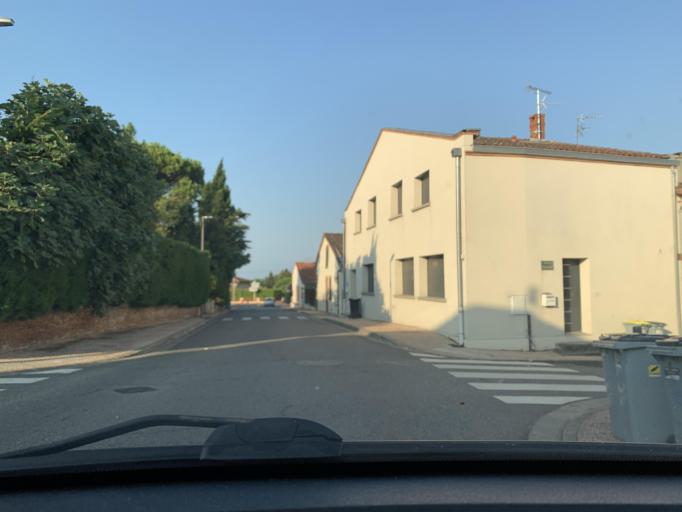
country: FR
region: Midi-Pyrenees
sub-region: Departement de la Haute-Garonne
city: Belberaud
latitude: 43.5233
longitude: 1.5889
